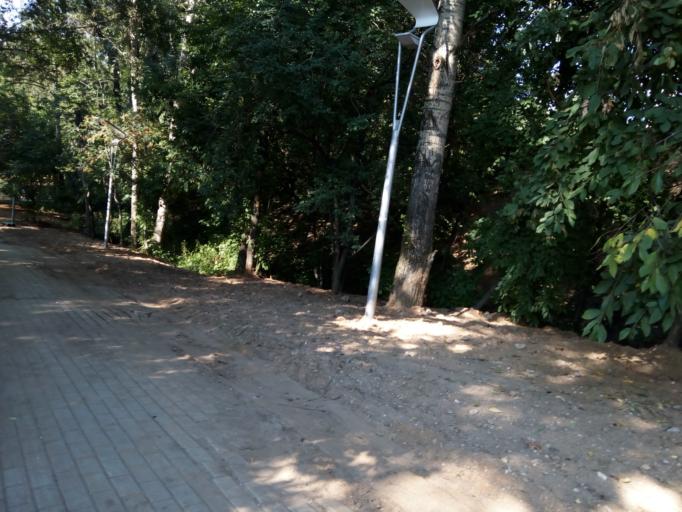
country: RU
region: Moskovskaya
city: Levoberezhnaya
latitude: 55.8785
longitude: 37.4664
